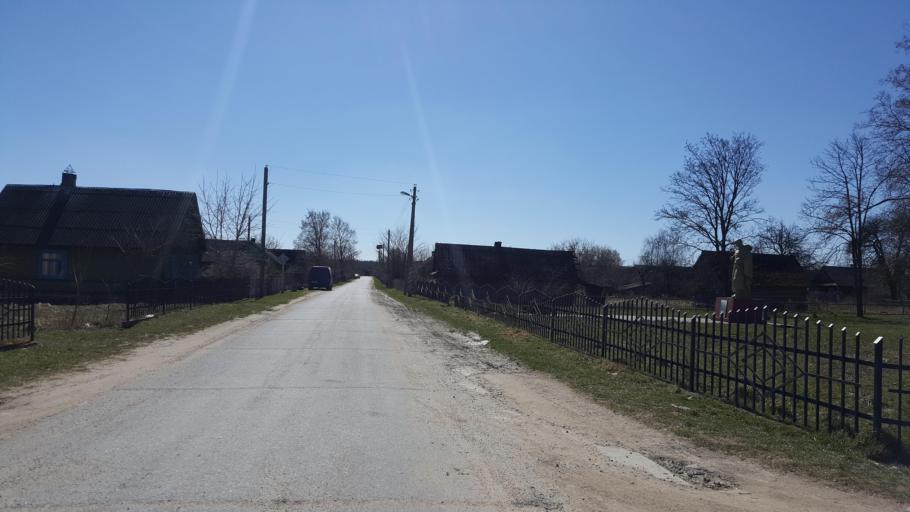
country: BY
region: Brest
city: Kamyanyets
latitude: 52.2902
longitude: 23.8599
